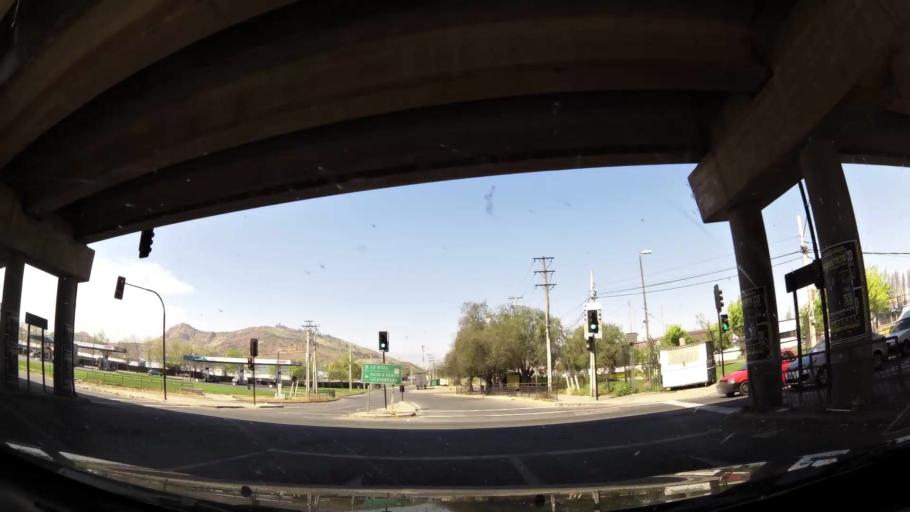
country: CL
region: Santiago Metropolitan
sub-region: Provincia de Santiago
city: Lo Prado
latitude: -33.3866
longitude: -70.7601
